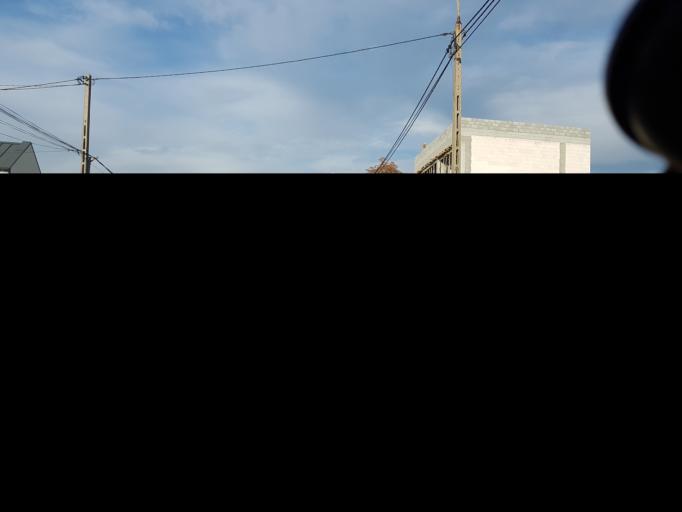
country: PL
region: Masovian Voivodeship
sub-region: Warszawa
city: Bemowo
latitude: 52.2862
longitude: 20.8846
